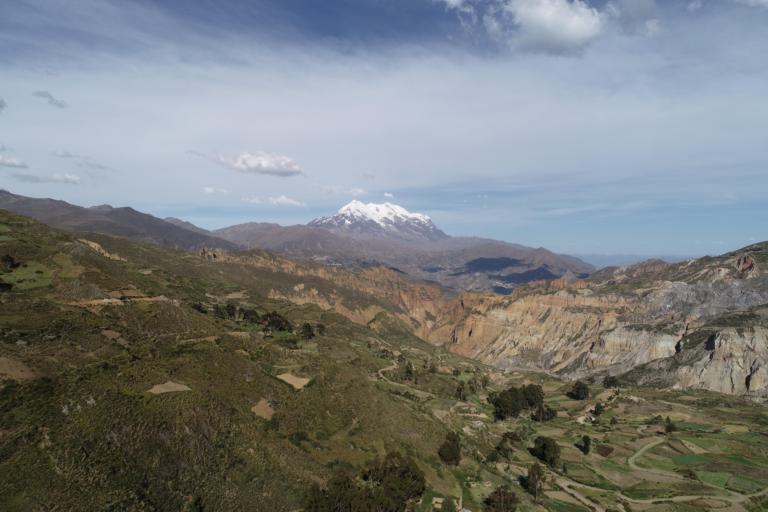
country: BO
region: La Paz
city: La Paz
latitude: -16.5491
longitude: -67.9930
